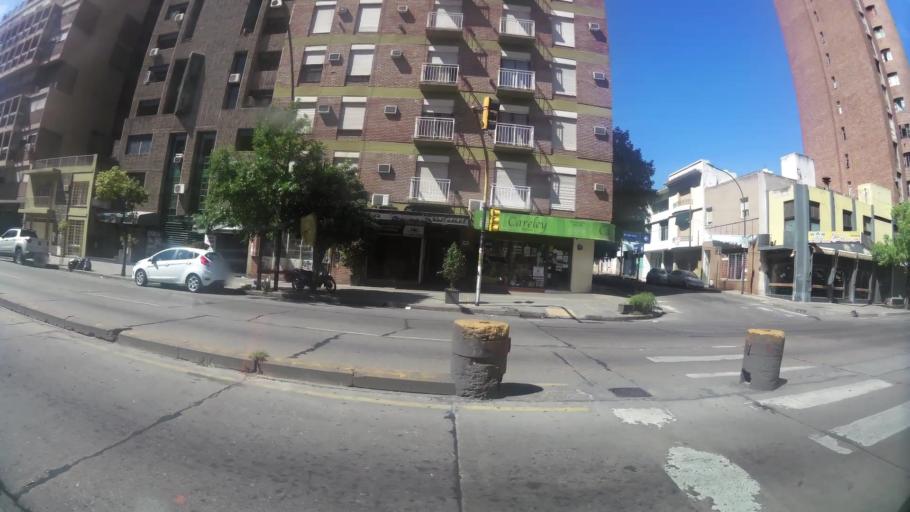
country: AR
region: Cordoba
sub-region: Departamento de Capital
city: Cordoba
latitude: -31.4178
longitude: -64.1926
